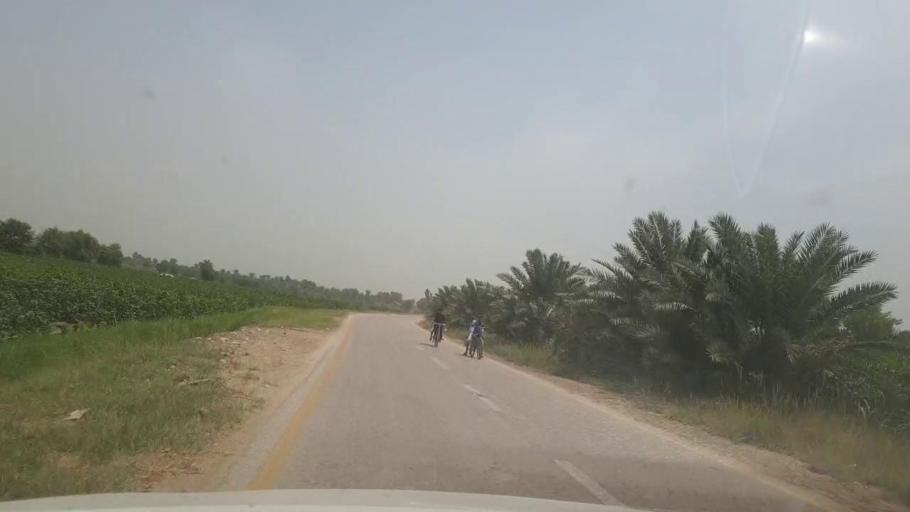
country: PK
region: Sindh
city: Kot Diji
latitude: 27.3766
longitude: 68.6527
